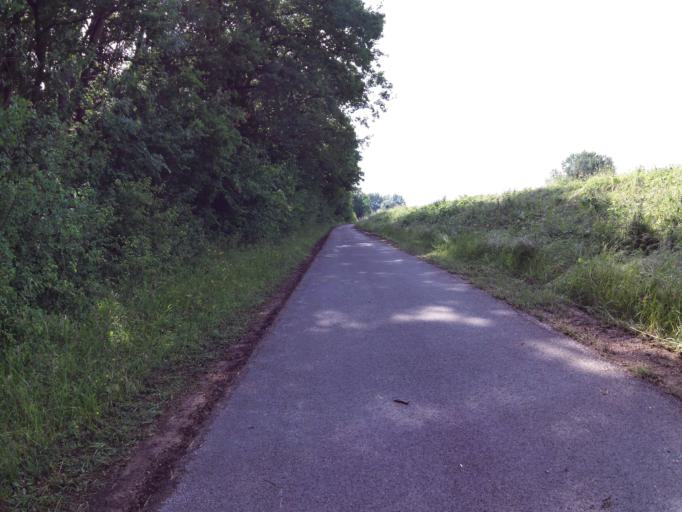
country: FR
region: Champagne-Ardenne
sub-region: Departement de l'Aube
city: Verrieres
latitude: 48.2690
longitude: 4.1707
